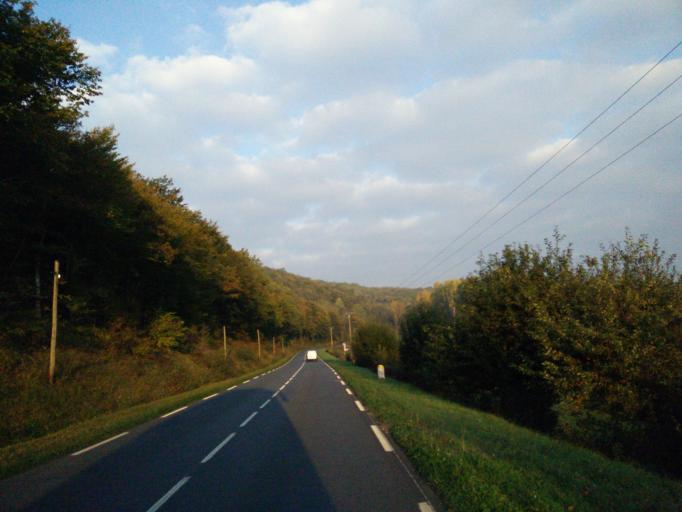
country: FR
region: Aquitaine
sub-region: Departement de la Dordogne
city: Le Bugue
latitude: 44.9664
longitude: 0.9654
